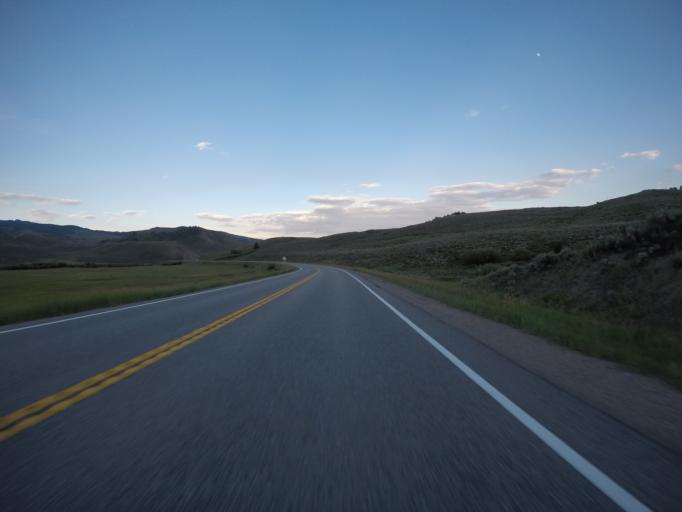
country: US
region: Colorado
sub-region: Grand County
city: Kremmling
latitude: 40.2939
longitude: -106.4906
